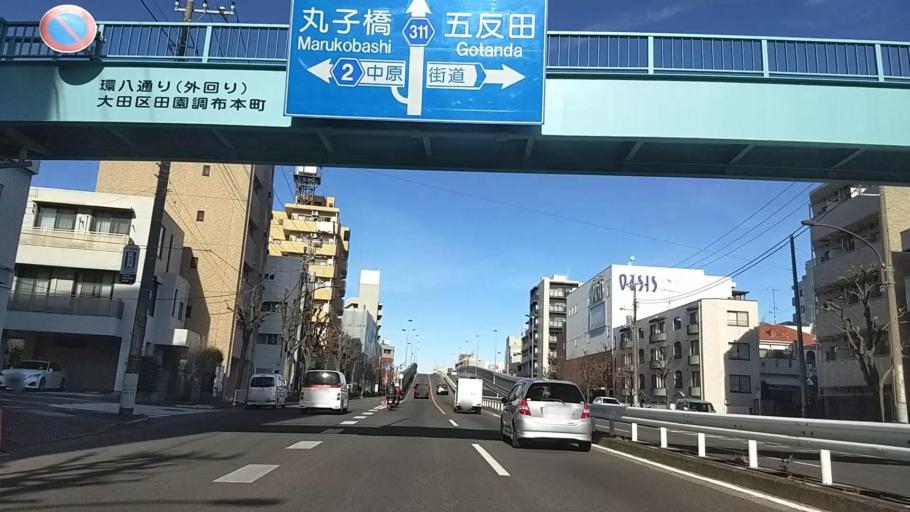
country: JP
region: Kanagawa
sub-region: Kawasaki-shi
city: Kawasaki
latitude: 35.5868
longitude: 139.6791
